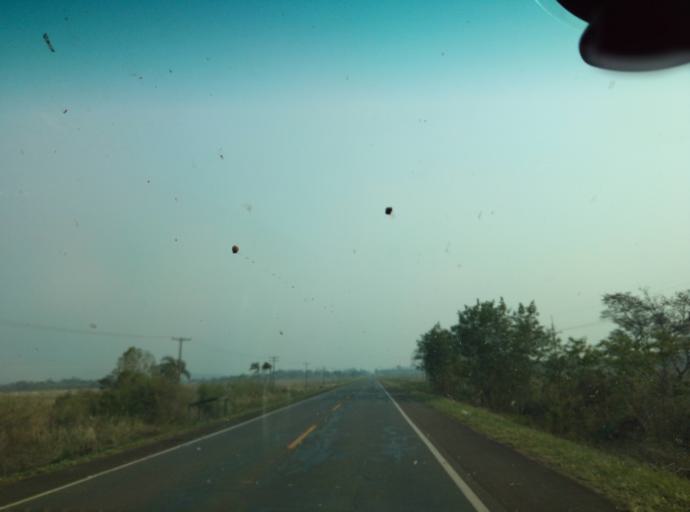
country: PY
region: Caaguazu
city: Carayao
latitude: -25.1296
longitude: -56.3534
